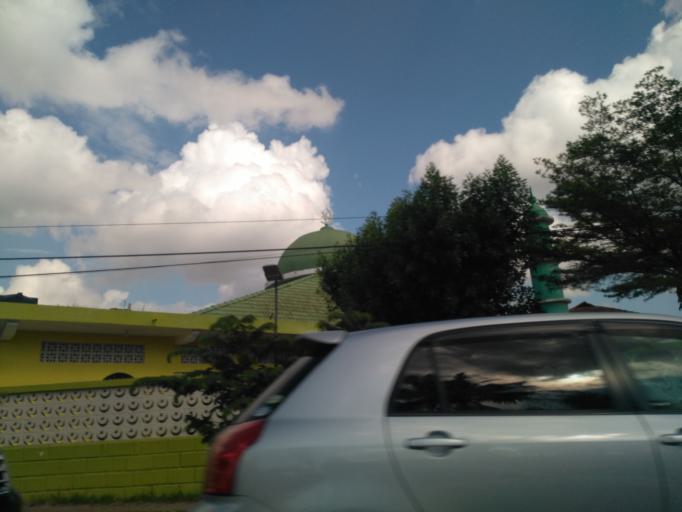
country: TZ
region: Dar es Salaam
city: Magomeni
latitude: -6.7577
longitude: 39.2449
